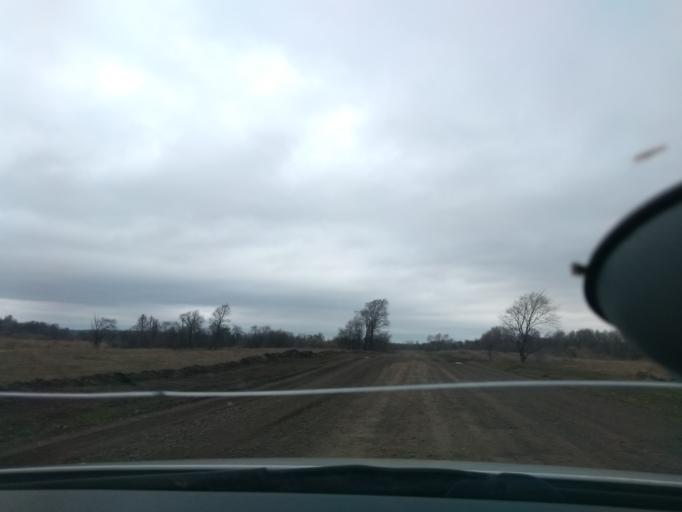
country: RU
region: Perm
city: Orda
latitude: 57.2359
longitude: 56.6109
